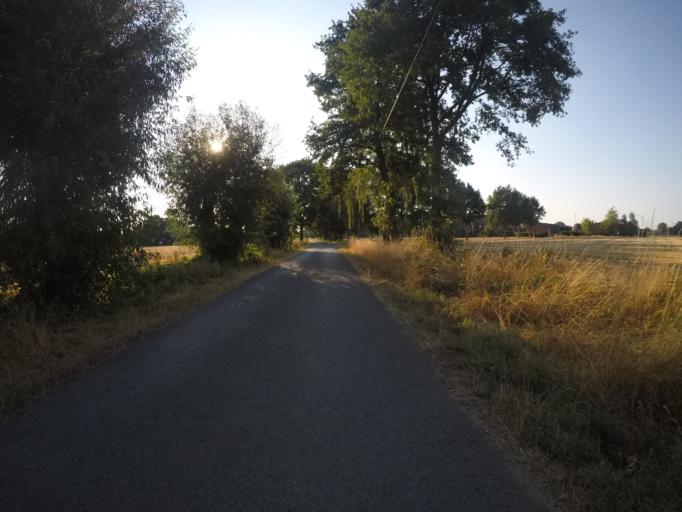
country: DE
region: North Rhine-Westphalia
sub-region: Regierungsbezirk Dusseldorf
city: Bocholt
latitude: 51.8494
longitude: 6.5771
